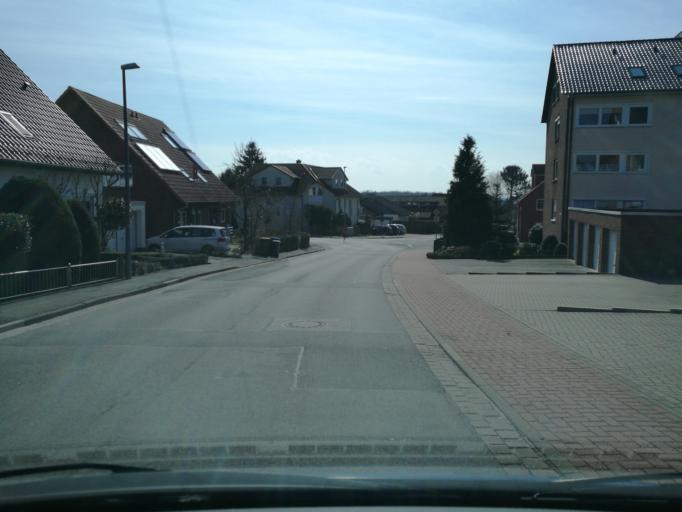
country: DE
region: Lower Saxony
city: Ronnenberg
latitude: 52.3702
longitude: 9.6519
